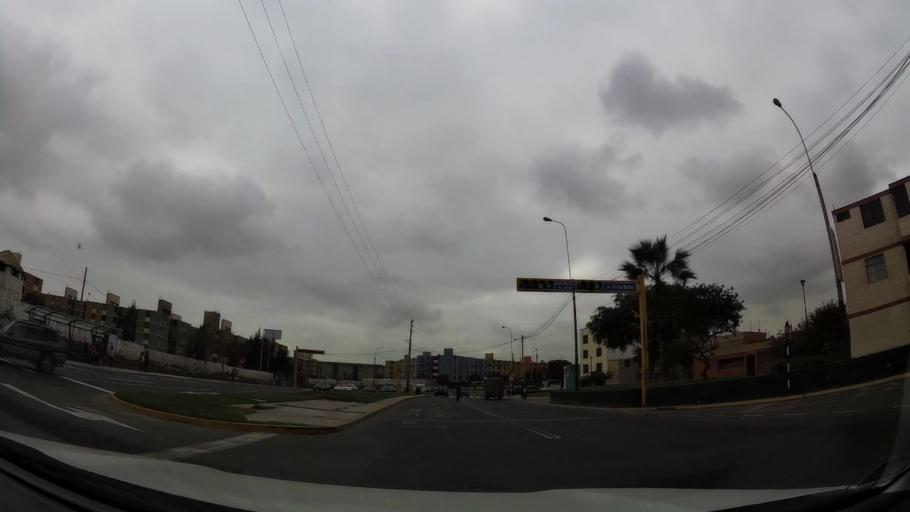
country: PE
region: Lima
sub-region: Lima
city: Surco
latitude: -12.1562
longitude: -76.9901
